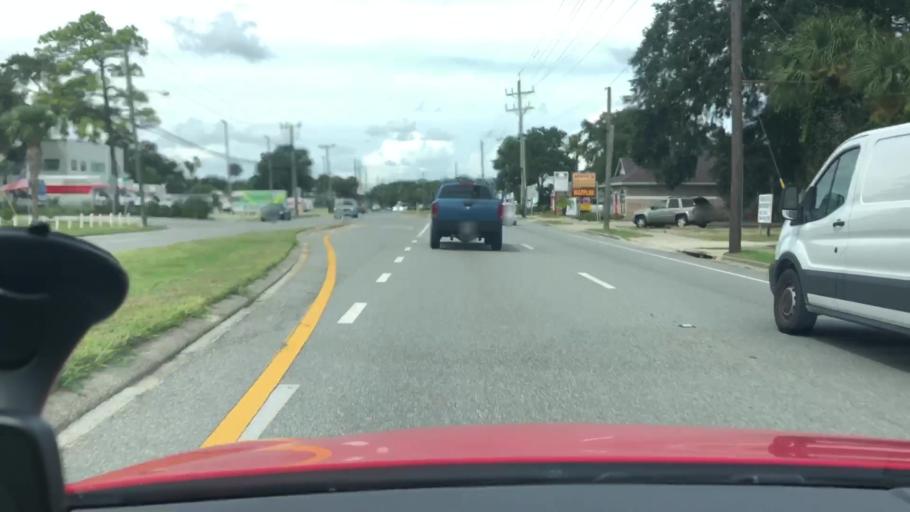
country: US
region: Florida
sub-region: Volusia County
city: New Smyrna Beach
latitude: 29.0448
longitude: -80.9346
